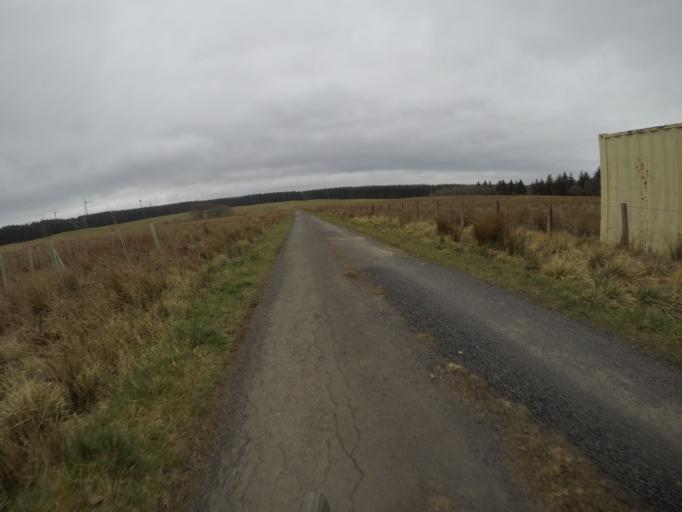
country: GB
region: Scotland
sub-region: East Ayrshire
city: Newmilns
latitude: 55.6629
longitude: -4.3477
